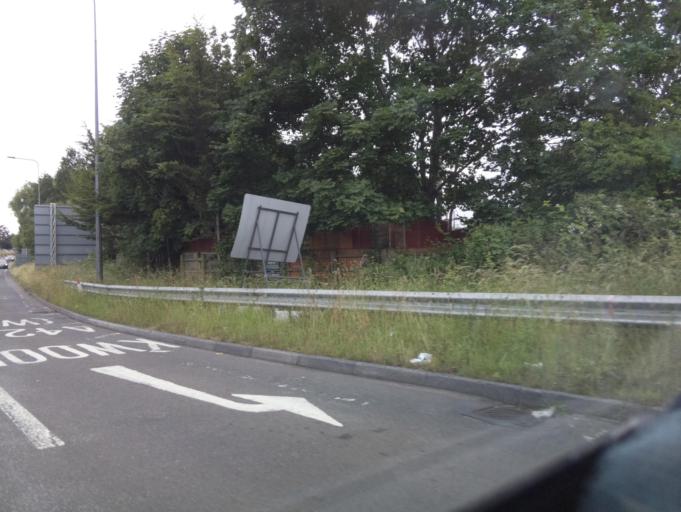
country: GB
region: England
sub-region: South Gloucestershire
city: Kingswood
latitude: 51.4592
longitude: -2.4823
